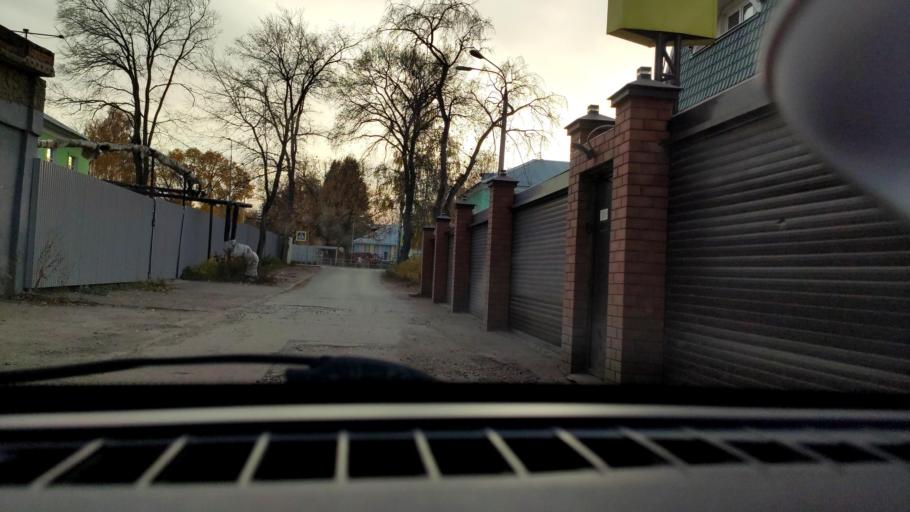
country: RU
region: Samara
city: Samara
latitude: 53.2674
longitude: 50.2412
